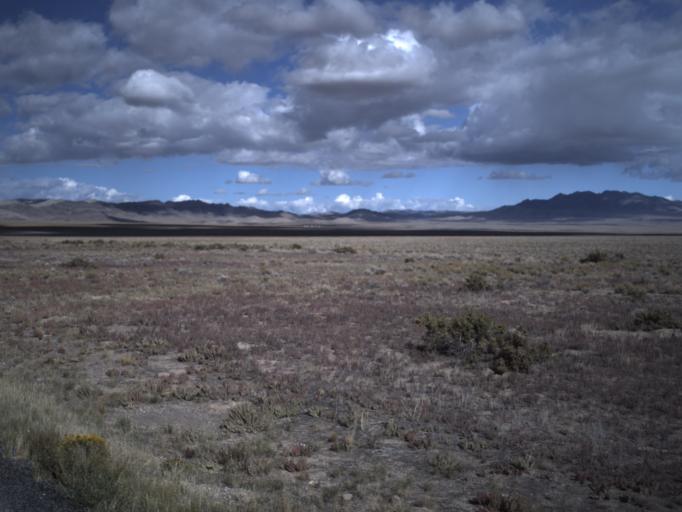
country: US
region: Utah
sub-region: Beaver County
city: Milford
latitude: 38.5438
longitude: -113.7128
